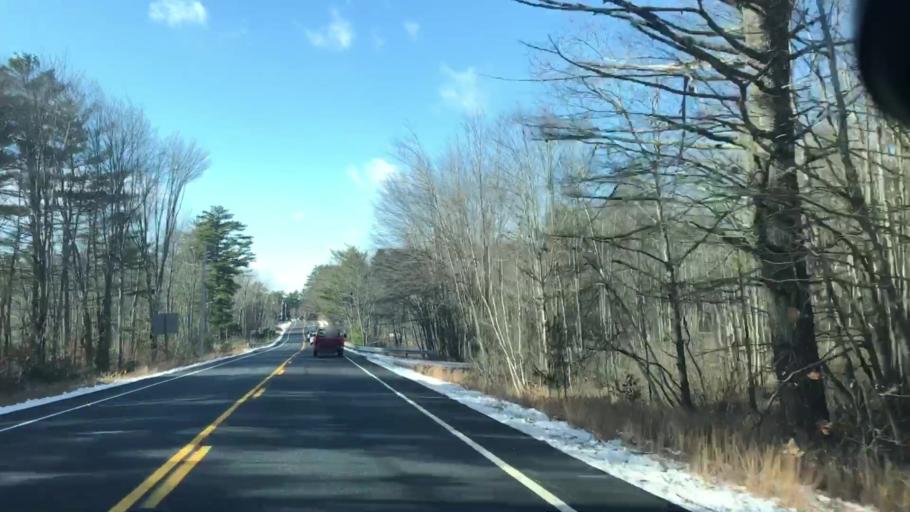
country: US
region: New Hampshire
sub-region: Carroll County
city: Effingham
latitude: 43.7942
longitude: -70.9860
